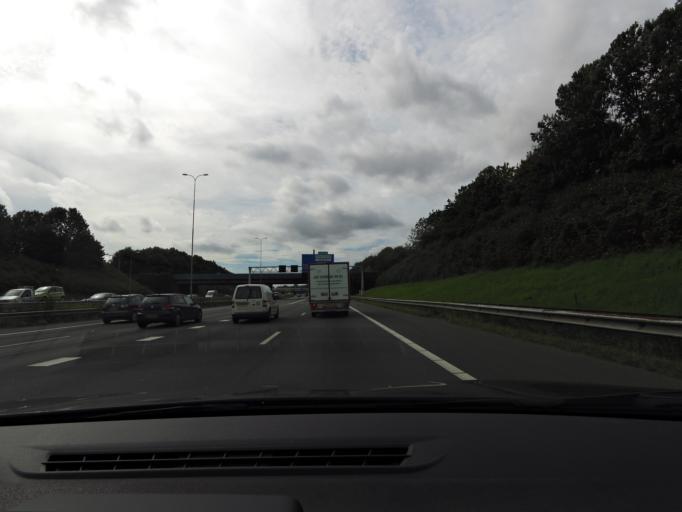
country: NL
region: Utrecht
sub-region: Gemeente Utrecht
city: Lunetten
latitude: 52.0691
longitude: 5.1484
